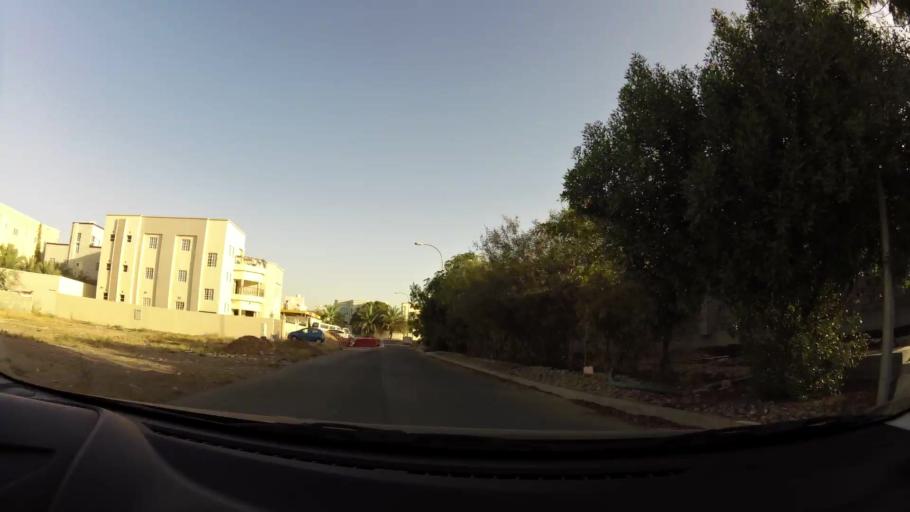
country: OM
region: Muhafazat Masqat
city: As Sib al Jadidah
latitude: 23.6091
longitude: 58.2295
